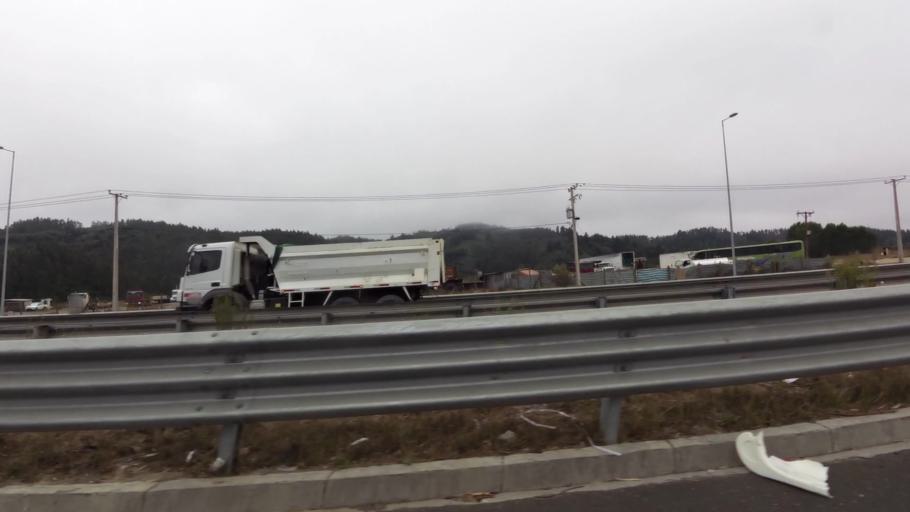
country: CL
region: Biobio
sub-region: Provincia de Concepcion
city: Concepcion
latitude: -36.8181
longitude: -73.0118
